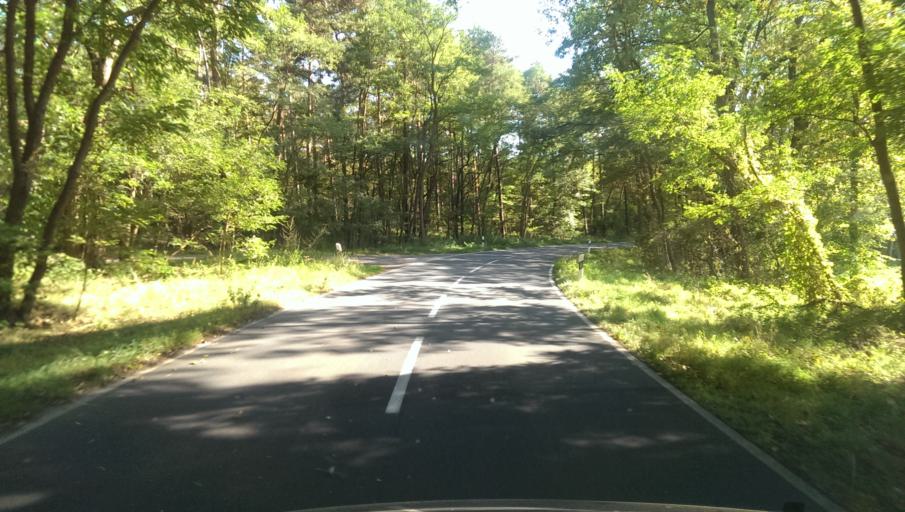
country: DE
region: Brandenburg
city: Halbe
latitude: 52.0866
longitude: 13.7302
